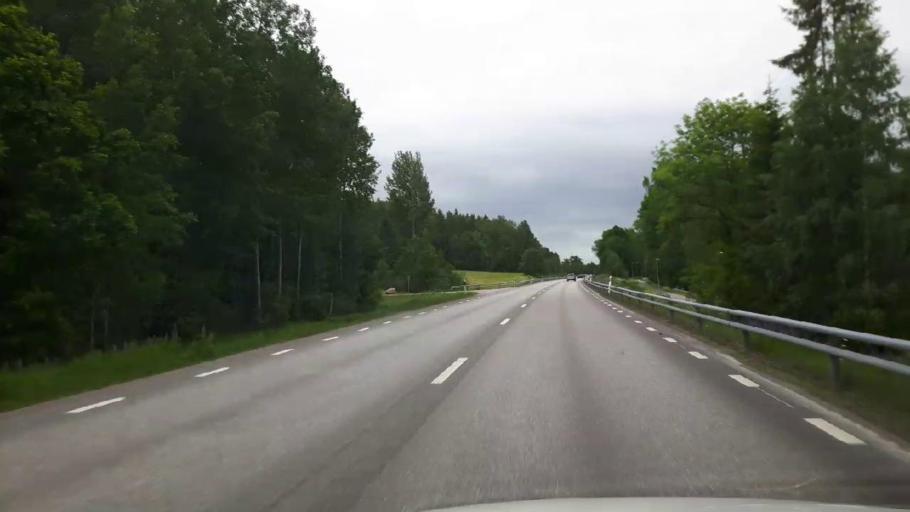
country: SE
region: Vaestmanland
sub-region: Kopings Kommun
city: Kolsva
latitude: 59.5608
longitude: 15.8912
